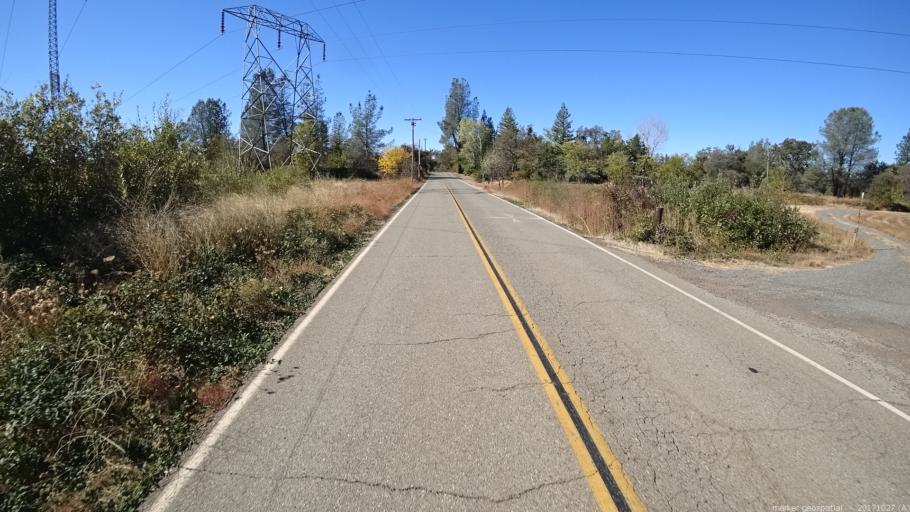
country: US
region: California
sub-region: Shasta County
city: Bella Vista
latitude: 40.6847
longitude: -122.0277
